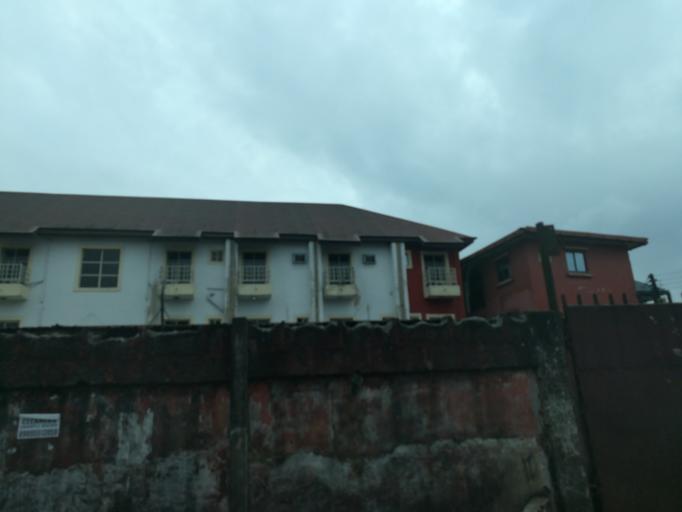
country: NG
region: Rivers
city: Port Harcourt
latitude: 4.8289
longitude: 7.0234
